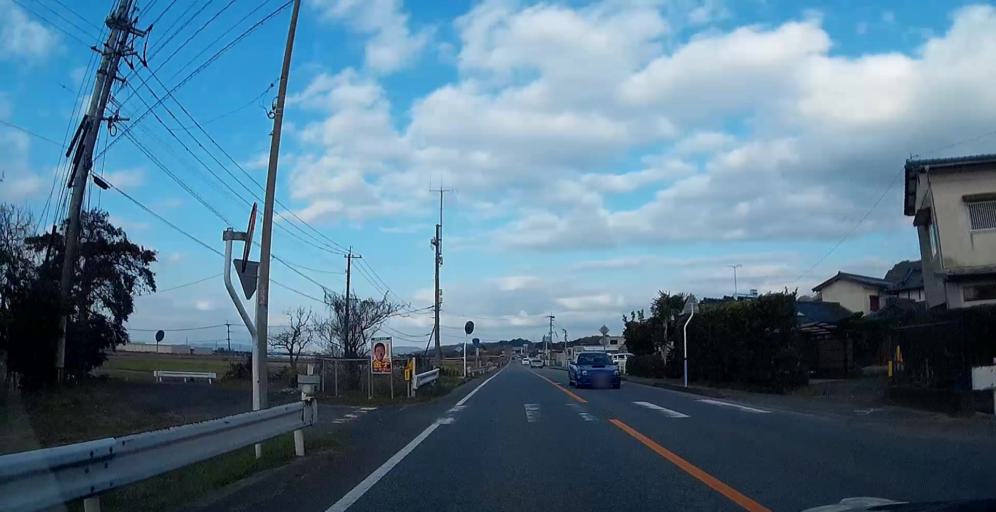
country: JP
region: Kumamoto
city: Yatsushiro
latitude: 32.5330
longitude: 130.6655
